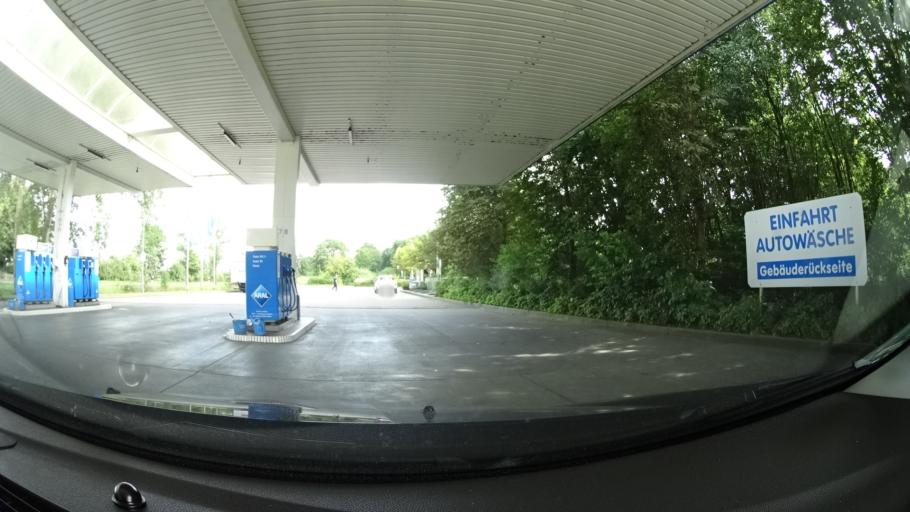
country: DE
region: Schleswig-Holstein
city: Risum-Lindholm
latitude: 54.7604
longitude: 8.8774
